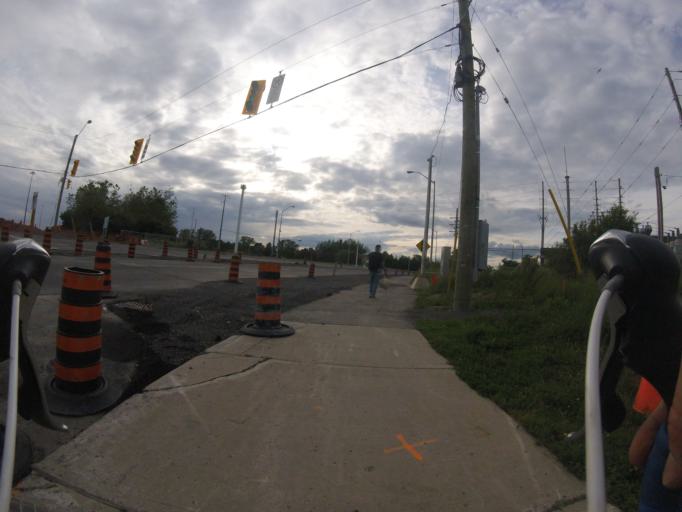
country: CA
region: Ontario
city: Bells Corners
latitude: 45.3449
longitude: -75.8147
